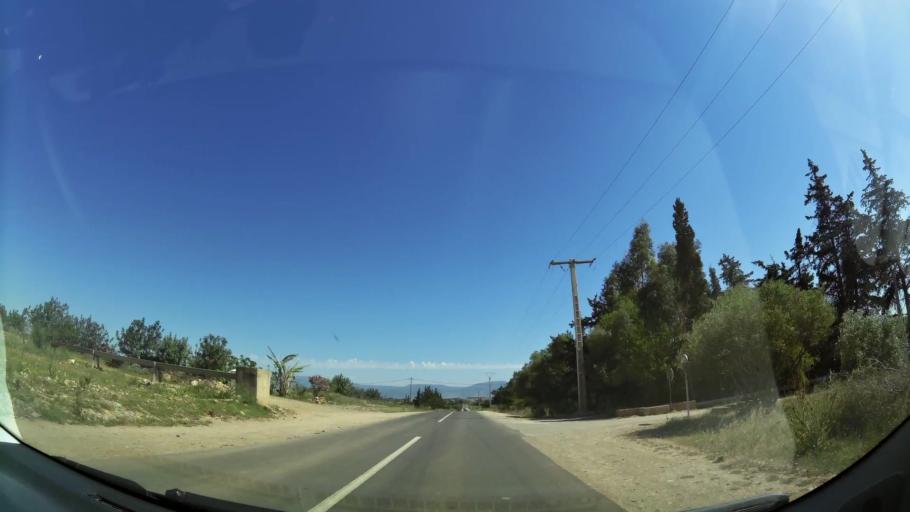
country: MA
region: Oriental
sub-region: Berkane-Taourirt
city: Madagh
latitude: 35.0269
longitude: -2.4114
